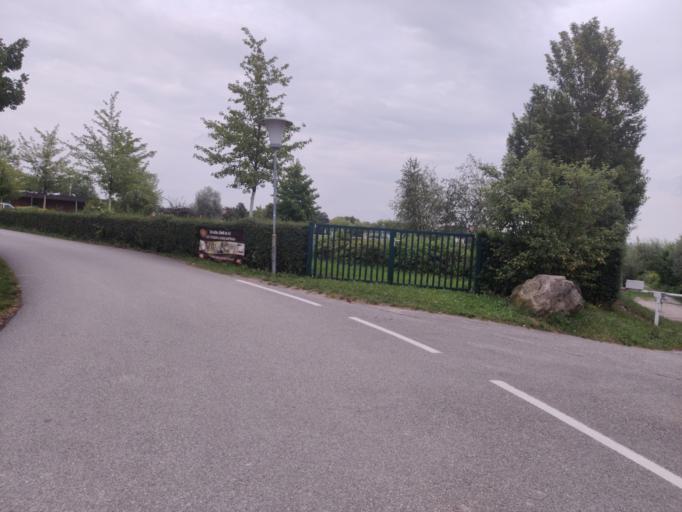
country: AT
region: Upper Austria
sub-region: Politischer Bezirk Perg
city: Perg
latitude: 48.2274
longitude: 14.5782
